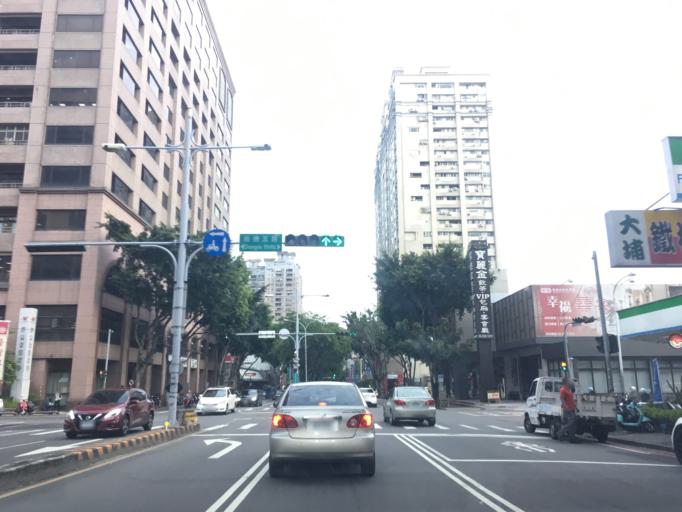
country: TW
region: Taiwan
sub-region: Taichung City
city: Taichung
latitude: 24.1794
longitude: 120.6860
